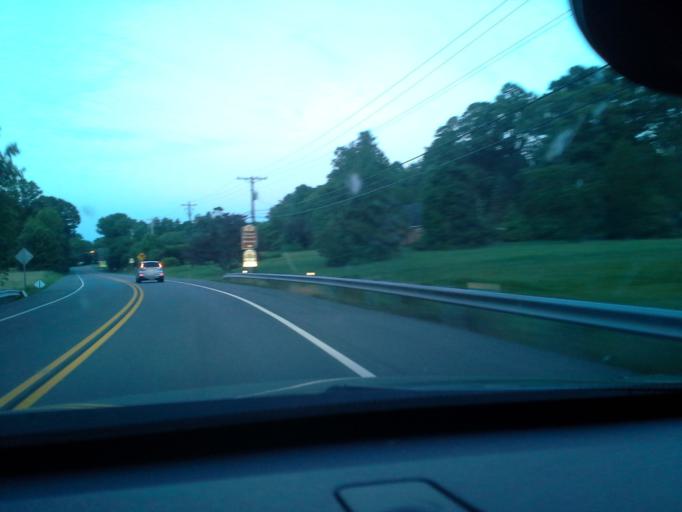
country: US
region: Maryland
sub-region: Calvert County
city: Huntingtown
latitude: 38.6152
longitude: -76.5536
